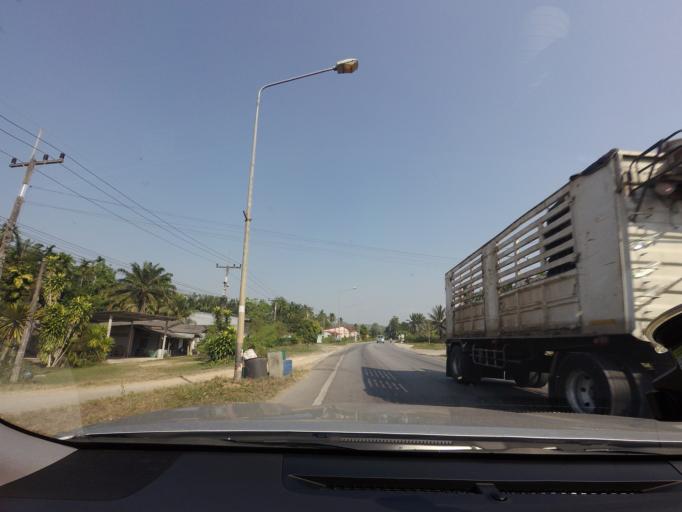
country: TH
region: Surat Thani
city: Chai Buri
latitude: 8.6024
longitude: 99.0148
